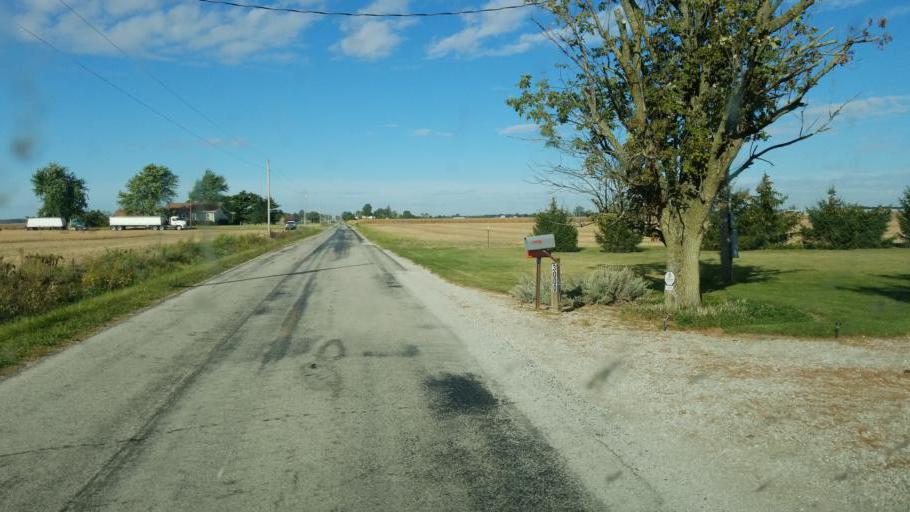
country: US
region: Ohio
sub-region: Marion County
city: Marion
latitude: 40.6885
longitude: -83.0489
